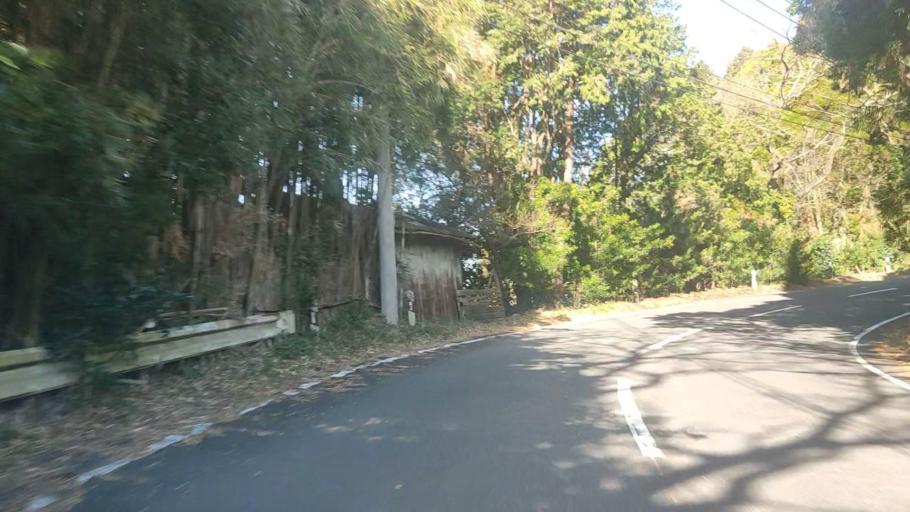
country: JP
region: Kagoshima
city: Kokubu-matsuki
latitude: 31.6673
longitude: 130.8256
